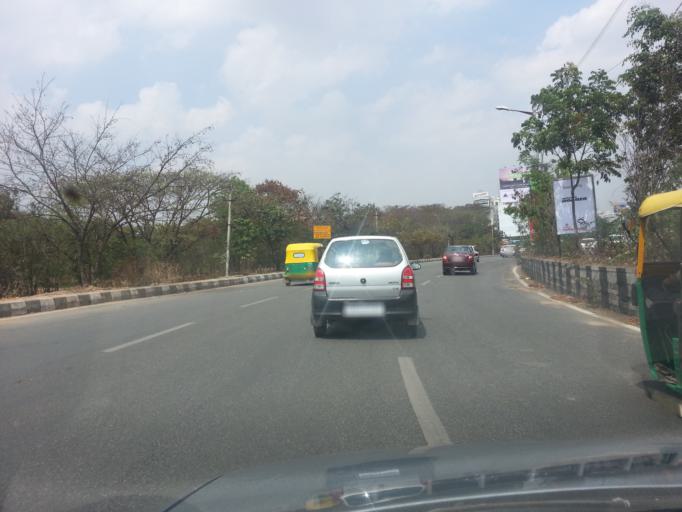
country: IN
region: Karnataka
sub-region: Bangalore Urban
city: Bangalore
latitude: 12.9501
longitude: 77.6390
